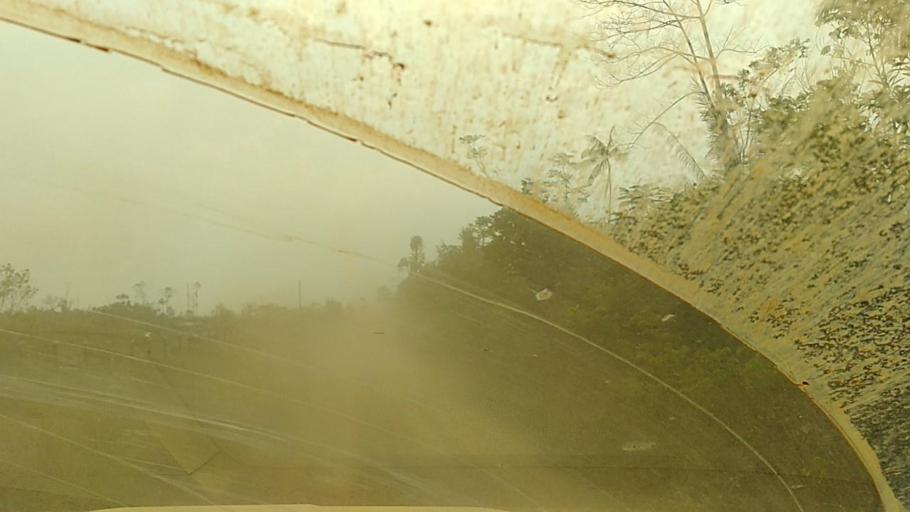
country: BR
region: Rondonia
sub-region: Porto Velho
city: Porto Velho
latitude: -8.7727
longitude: -63.2026
